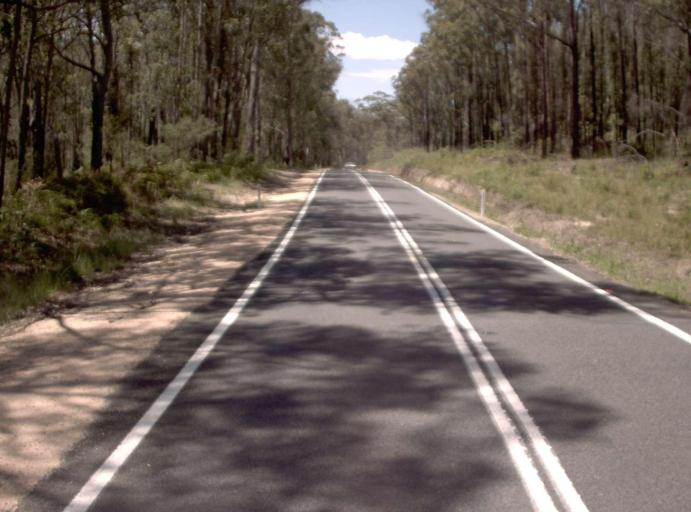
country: AU
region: New South Wales
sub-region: Bombala
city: Bombala
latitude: -37.6362
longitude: 148.8645
